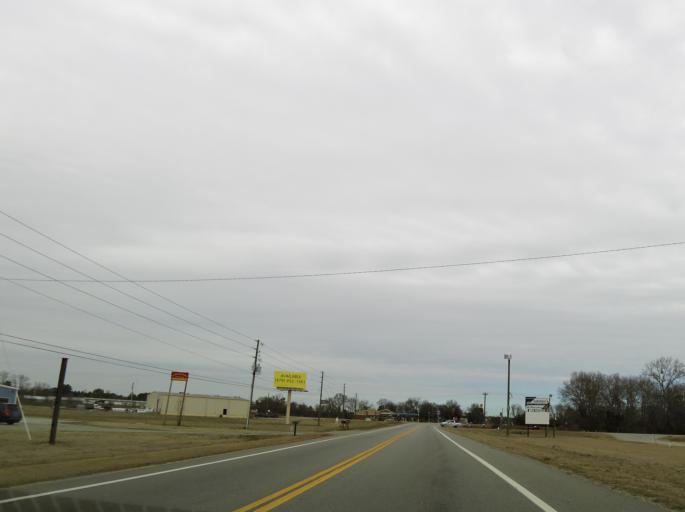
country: US
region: Georgia
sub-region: Peach County
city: Byron
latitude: 32.6079
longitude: -83.7492
